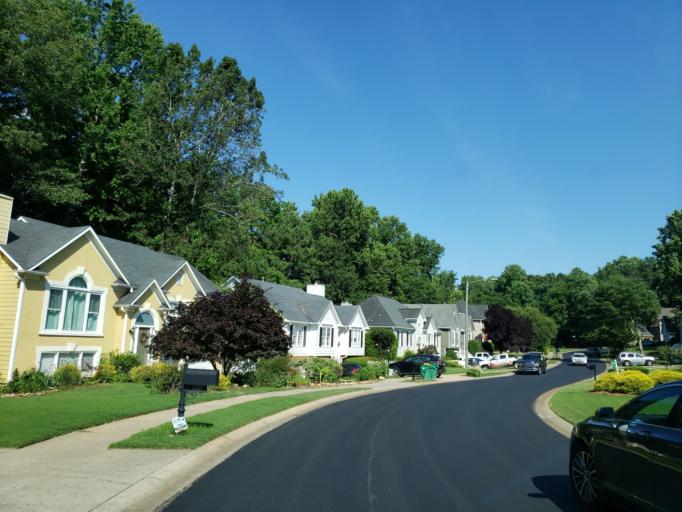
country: US
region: Georgia
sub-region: Cherokee County
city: Woodstock
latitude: 34.1188
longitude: -84.5344
